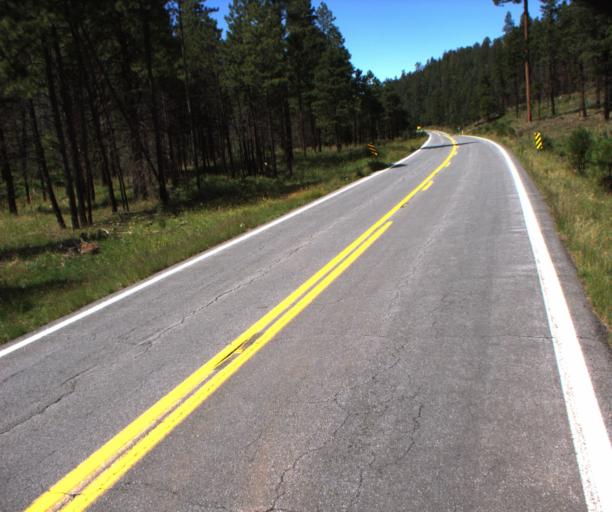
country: US
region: Arizona
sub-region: Apache County
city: Eagar
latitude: 33.7909
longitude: -109.1645
